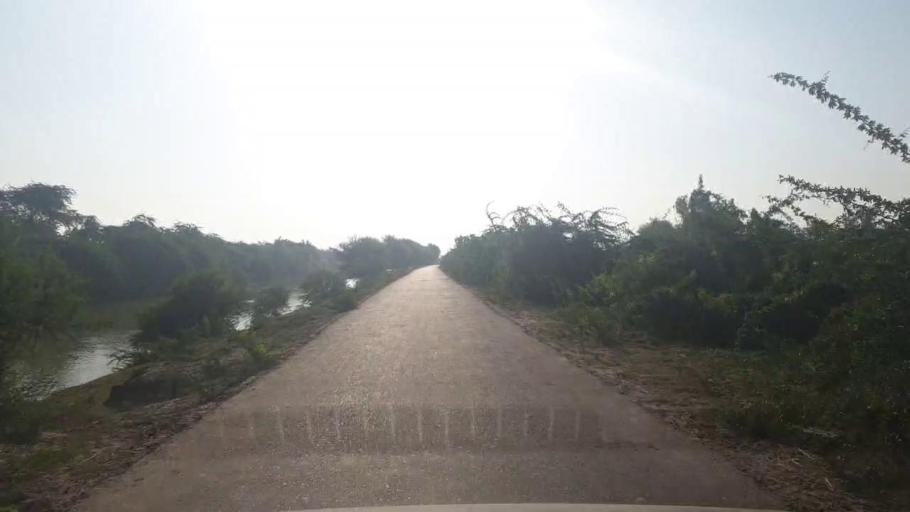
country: PK
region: Sindh
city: Tando Bago
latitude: 24.7334
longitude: 68.9333
